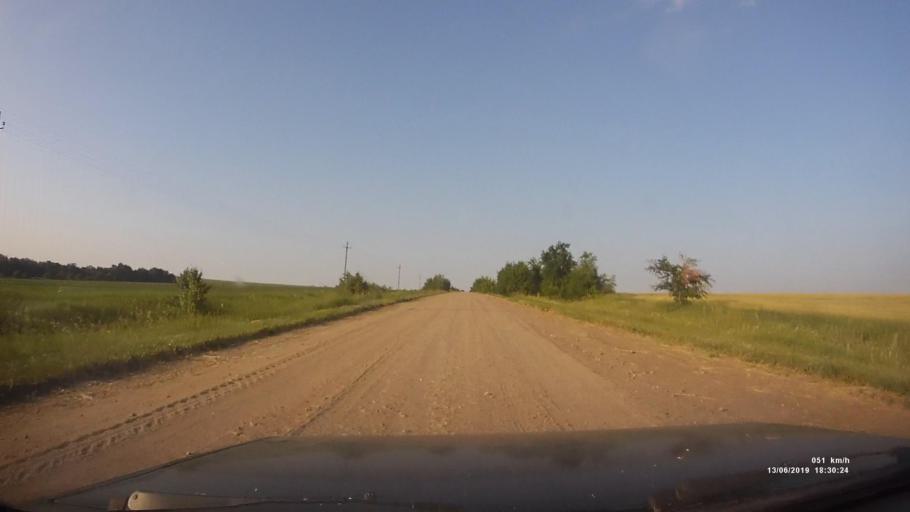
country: RU
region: Rostov
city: Kazanskaya
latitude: 49.8620
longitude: 41.3498
